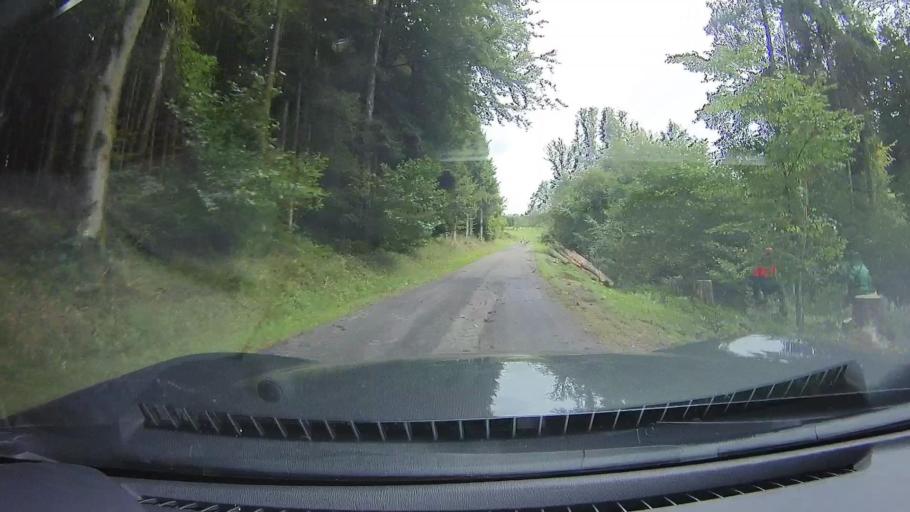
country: DE
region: Baden-Wuerttemberg
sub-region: Regierungsbezirk Stuttgart
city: Grosserlach
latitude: 49.0334
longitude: 9.5512
